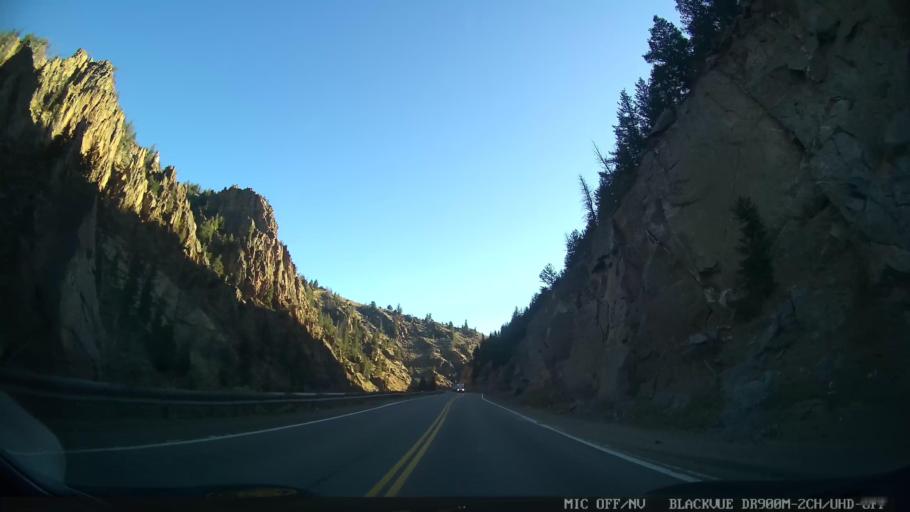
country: US
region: Colorado
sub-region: Grand County
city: Hot Sulphur Springs
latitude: 40.0625
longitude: -106.1246
